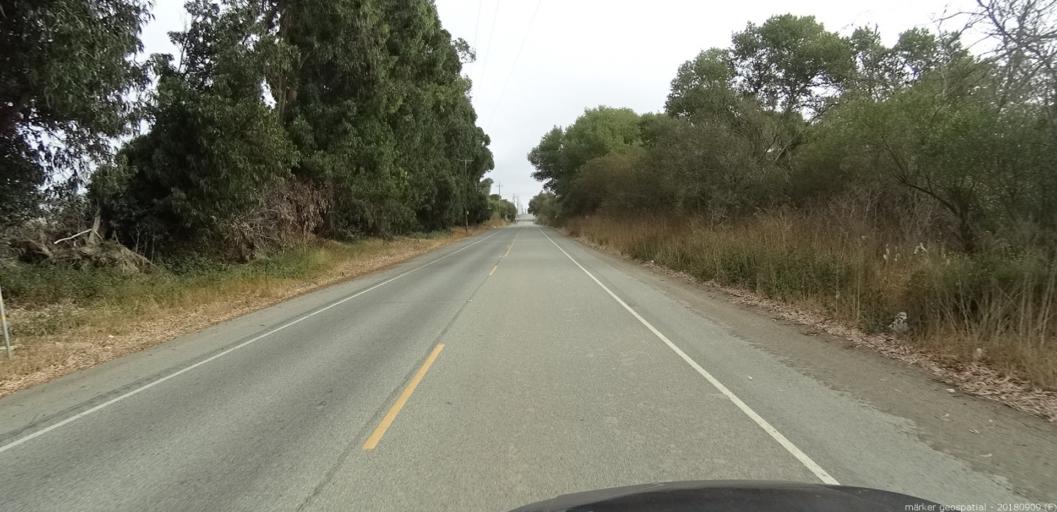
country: US
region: California
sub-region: Monterey County
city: Salinas
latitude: 36.6446
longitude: -121.7041
